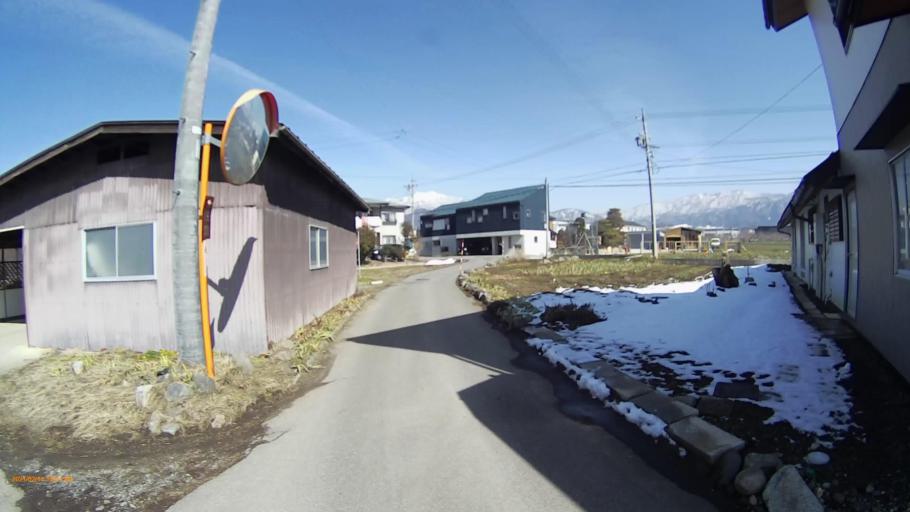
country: JP
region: Nagano
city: Nakano
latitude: 36.7530
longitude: 138.3552
